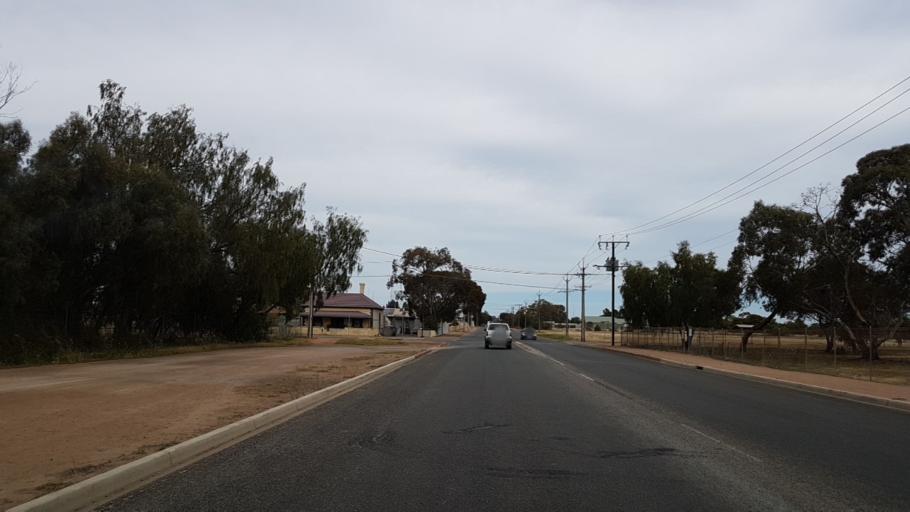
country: AU
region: South Australia
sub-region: Port Pirie City and Dists
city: Port Pirie
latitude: -33.1846
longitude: 137.9976
